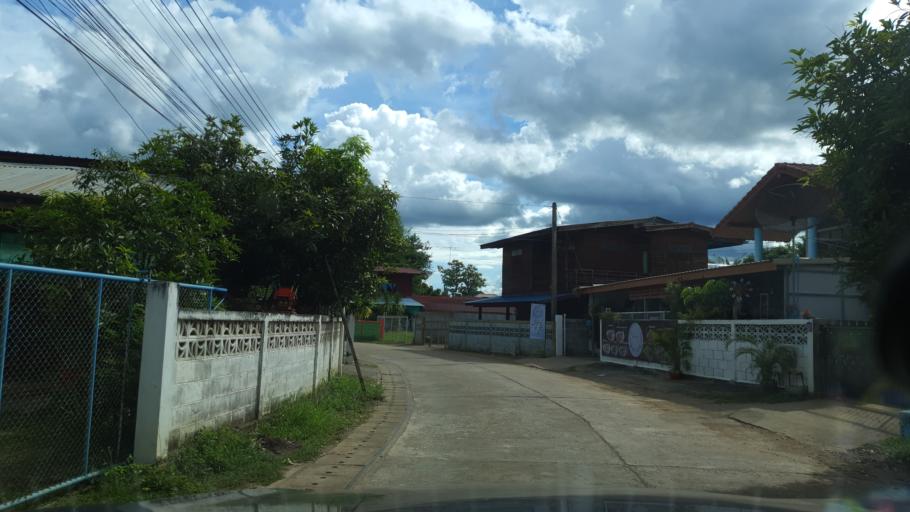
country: TH
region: Sukhothai
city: Thung Saliam
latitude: 17.3179
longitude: 99.5573
